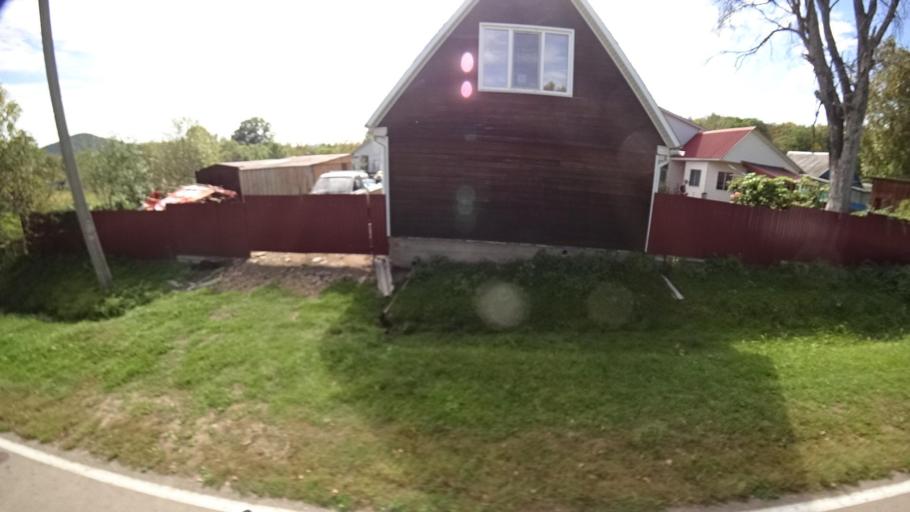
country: RU
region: Primorskiy
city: Yakovlevka
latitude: 44.3985
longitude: 133.5994
